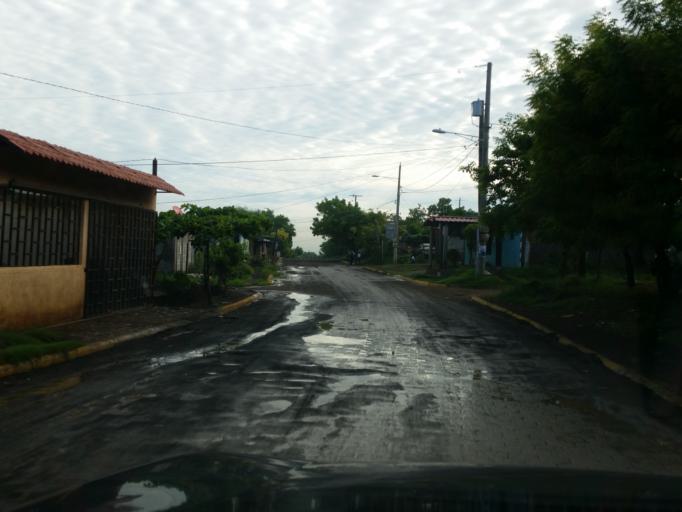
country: NI
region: Managua
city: Managua
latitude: 12.1093
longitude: -86.2094
